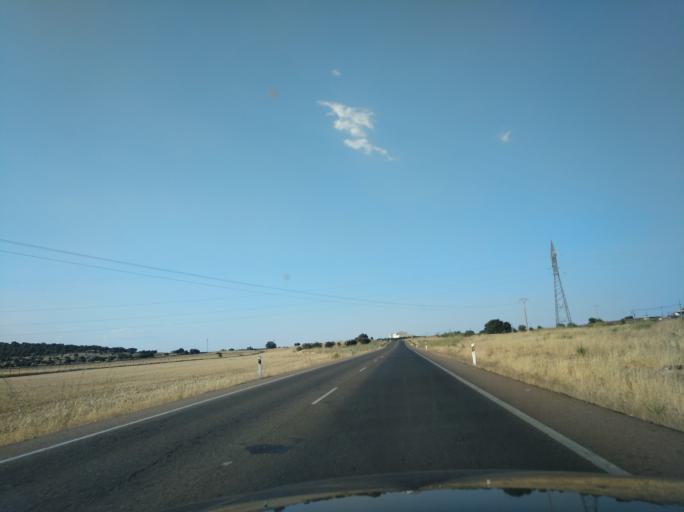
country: ES
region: Extremadura
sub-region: Provincia de Badajoz
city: Olivenza
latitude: 38.7009
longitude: -7.0886
